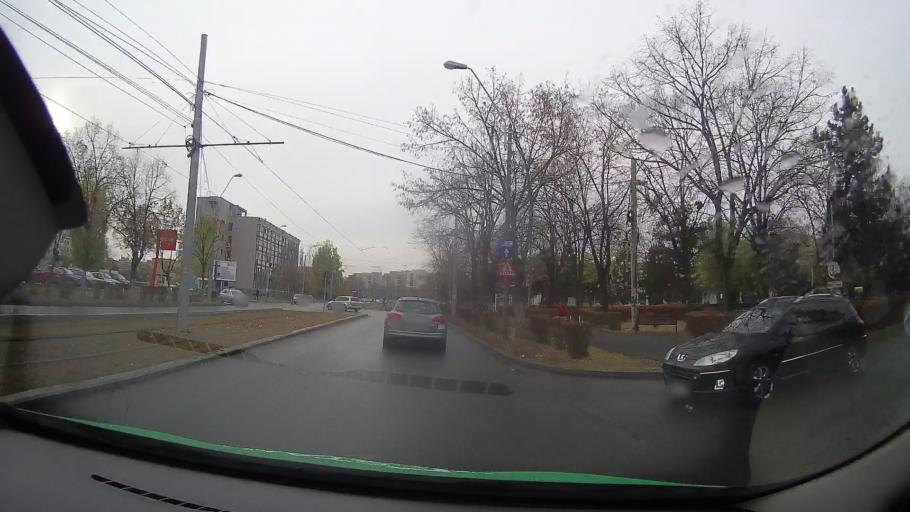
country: RO
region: Prahova
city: Ploiesti
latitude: 44.9351
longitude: 25.9895
